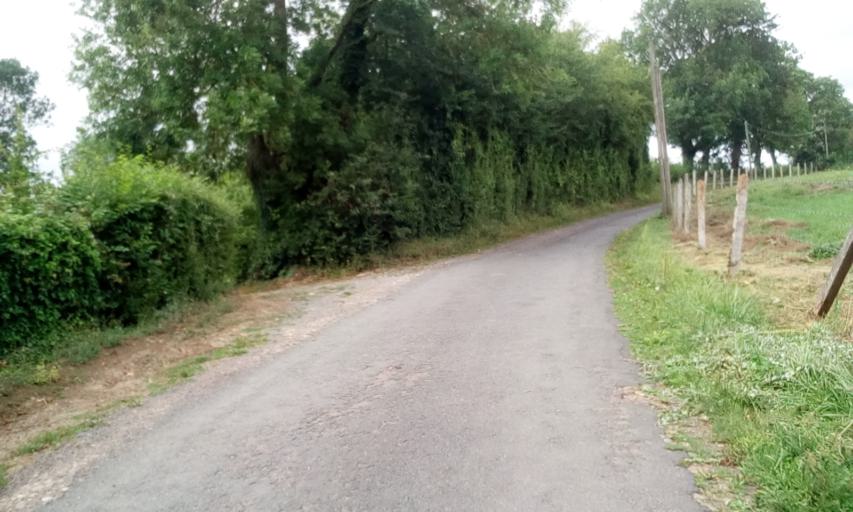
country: FR
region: Lower Normandy
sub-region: Departement du Calvados
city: Tilly-sur-Seulles
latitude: 49.2143
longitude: -0.6233
